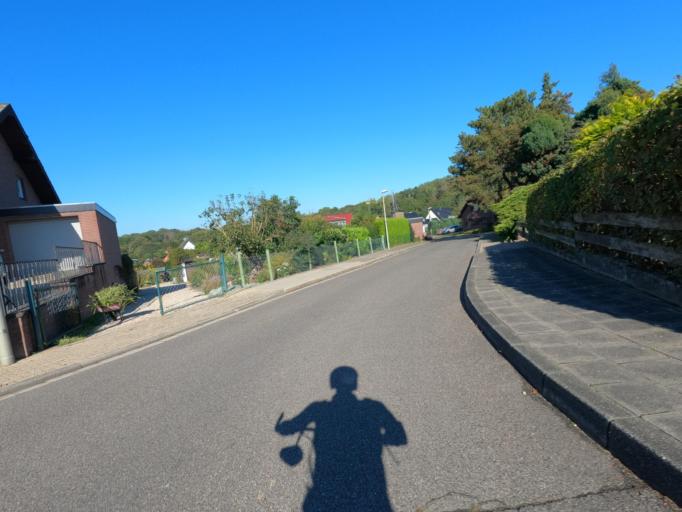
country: DE
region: North Rhine-Westphalia
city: Erkelenz
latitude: 51.0342
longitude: 6.2873
